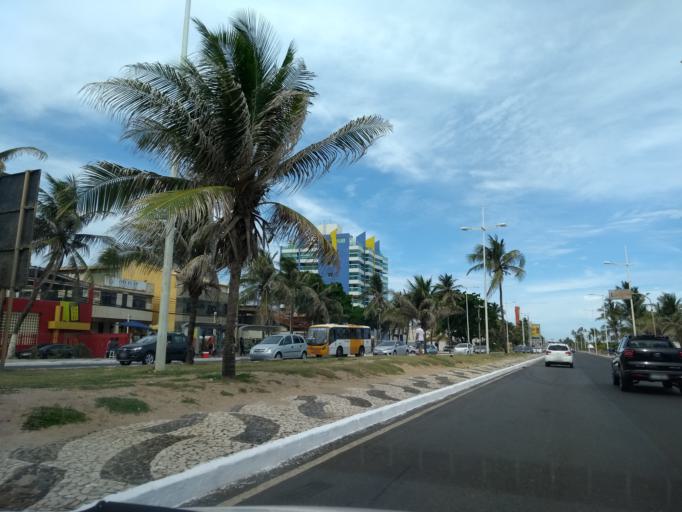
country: BR
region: Bahia
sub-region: Lauro De Freitas
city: Lauro de Freitas
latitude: -12.9544
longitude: -38.3831
